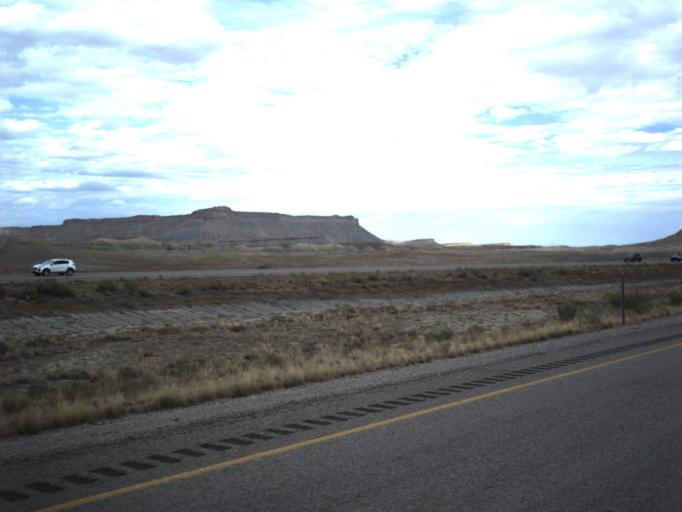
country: US
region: Utah
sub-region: Grand County
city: Moab
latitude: 38.9319
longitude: -110.0163
